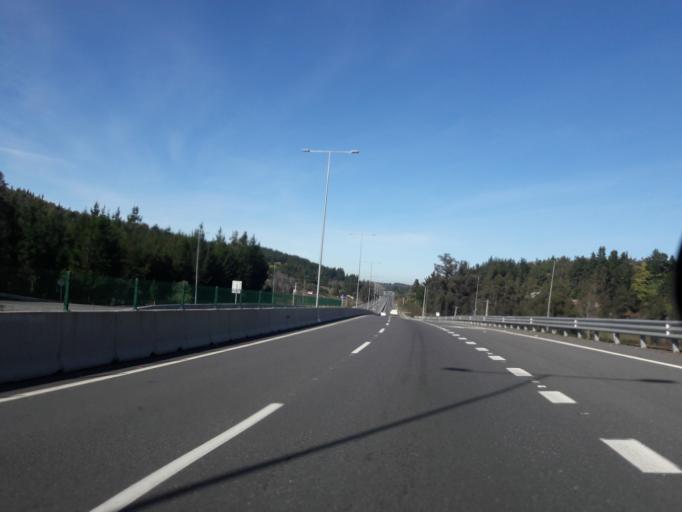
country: CL
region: Biobio
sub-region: Provincia de Biobio
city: Yumbel
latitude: -36.9365
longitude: -72.7610
